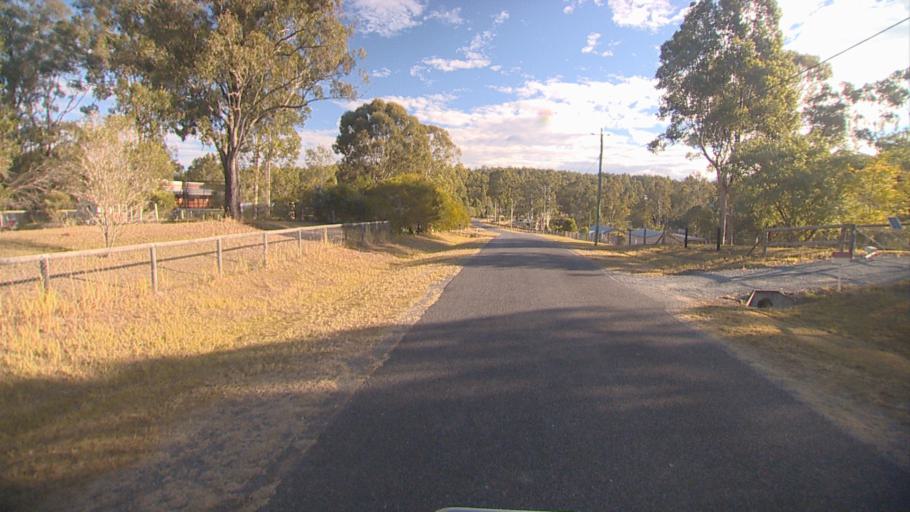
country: AU
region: Queensland
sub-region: Logan
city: Cedar Vale
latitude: -27.9315
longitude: 153.0628
